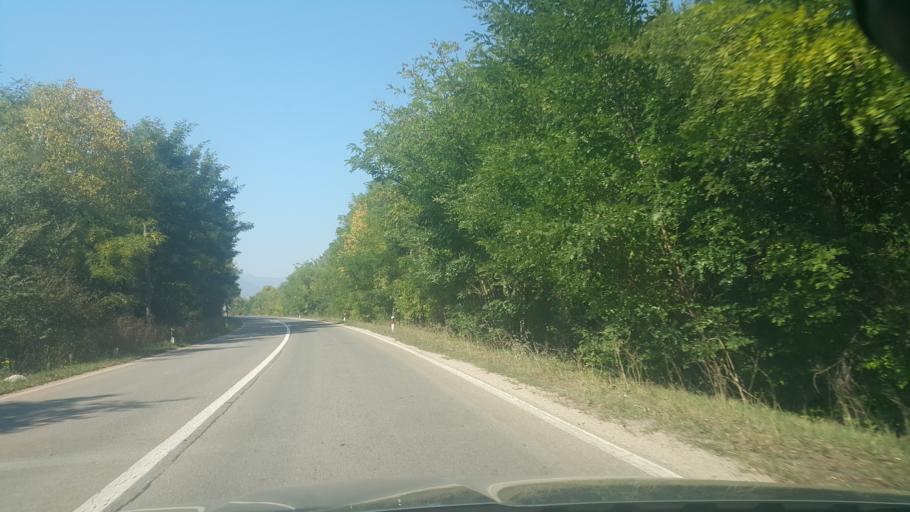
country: RS
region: Central Serbia
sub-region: Pirotski Okrug
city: Bela Palanka
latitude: 43.2604
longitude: 22.2593
